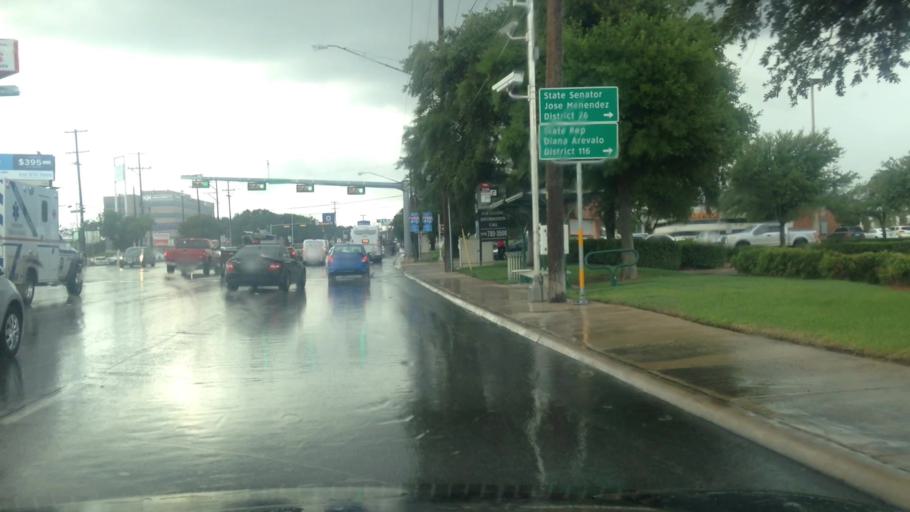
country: US
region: Texas
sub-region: Bexar County
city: Balcones Heights
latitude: 29.4922
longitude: -98.5532
